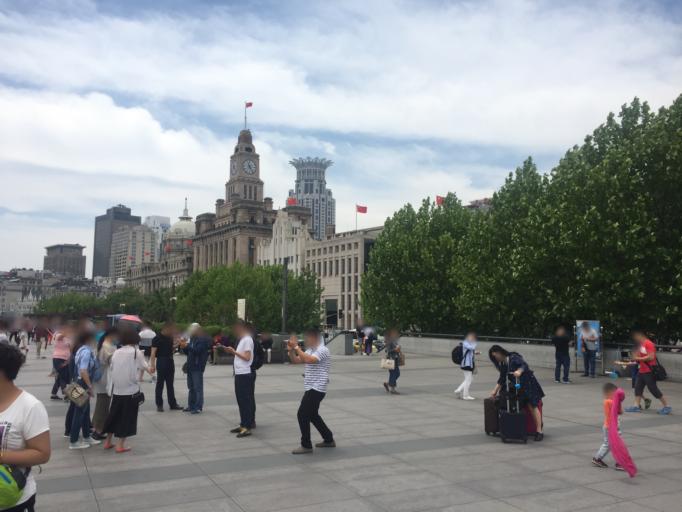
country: CN
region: Shanghai Shi
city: Hongkou
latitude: 31.2405
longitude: 121.4861
